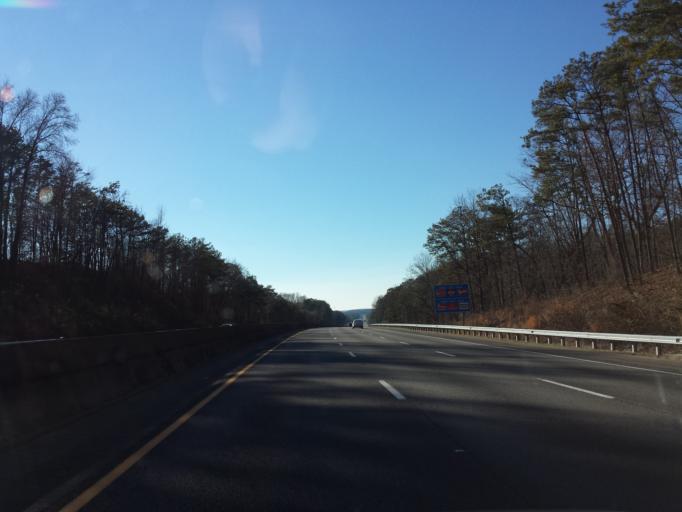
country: US
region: Alabama
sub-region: Saint Clair County
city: Moody
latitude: 33.5698
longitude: -86.4994
